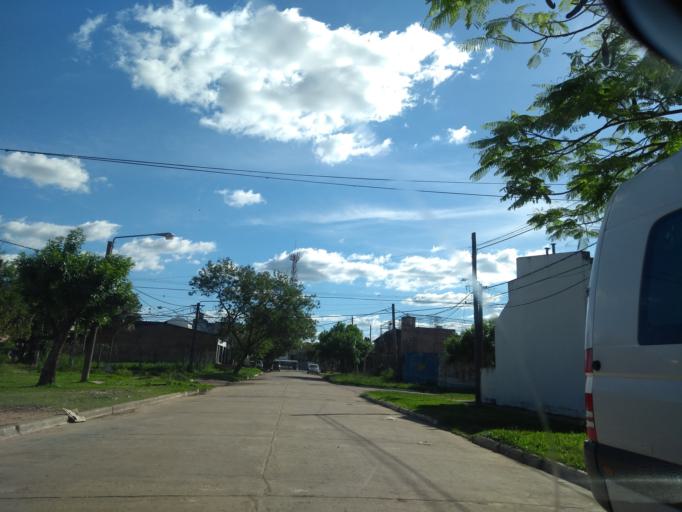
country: AR
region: Chaco
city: Barranqueras
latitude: -27.4740
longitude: -58.9584
